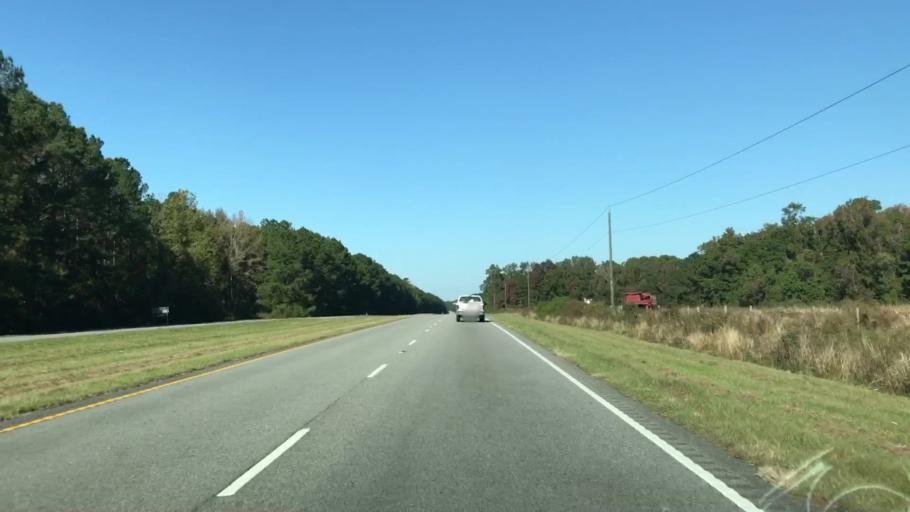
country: US
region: South Carolina
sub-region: Hampton County
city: Yemassee
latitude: 32.6130
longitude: -80.8133
